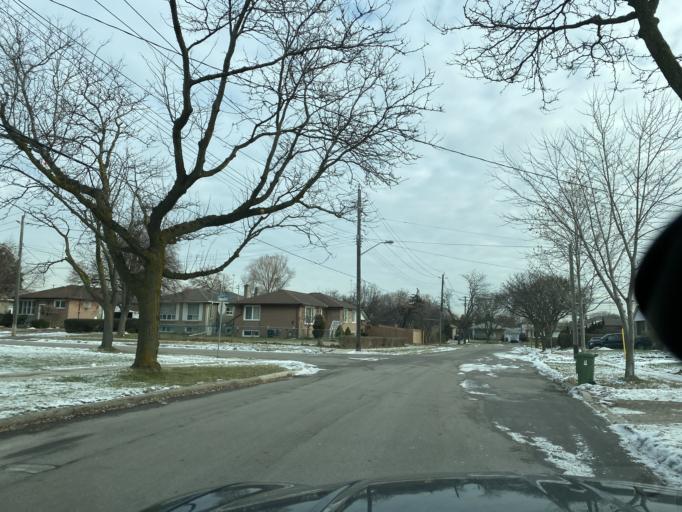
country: CA
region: Ontario
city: Etobicoke
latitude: 43.6685
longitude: -79.5819
